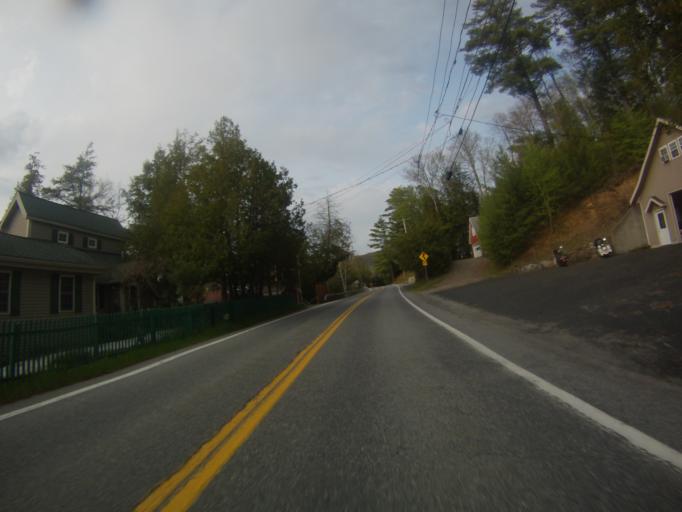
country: US
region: New York
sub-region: Warren County
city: Warrensburg
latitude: 43.7274
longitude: -73.6797
